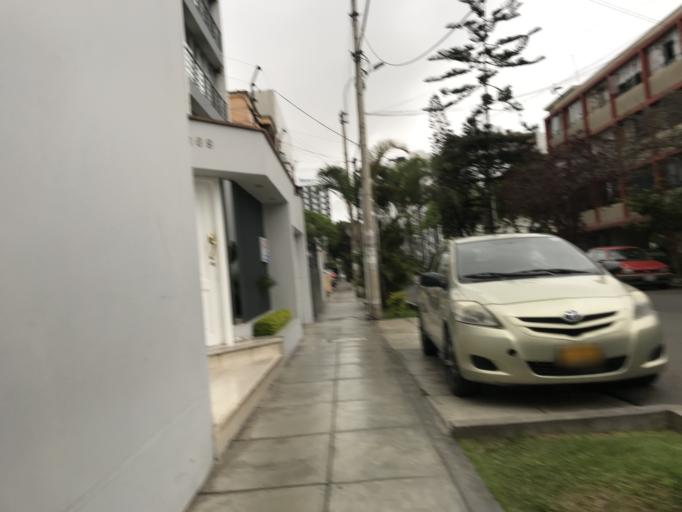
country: PE
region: Lima
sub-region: Lima
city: San Isidro
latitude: -12.0914
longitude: -77.0431
